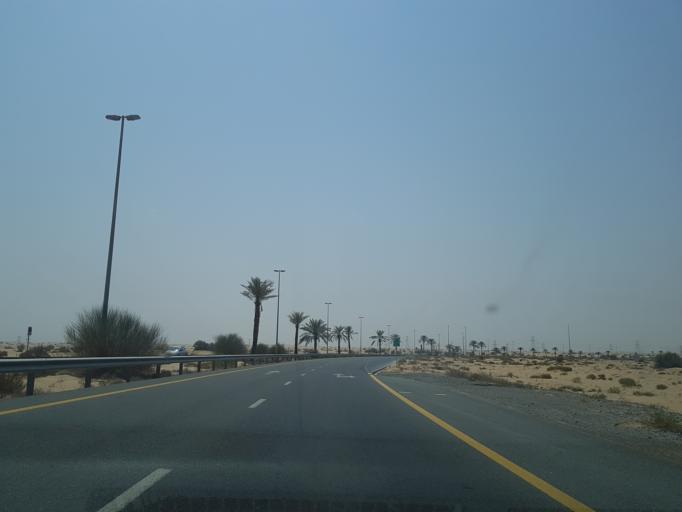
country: AE
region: Ash Shariqah
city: Sharjah
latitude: 25.1353
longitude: 55.4300
